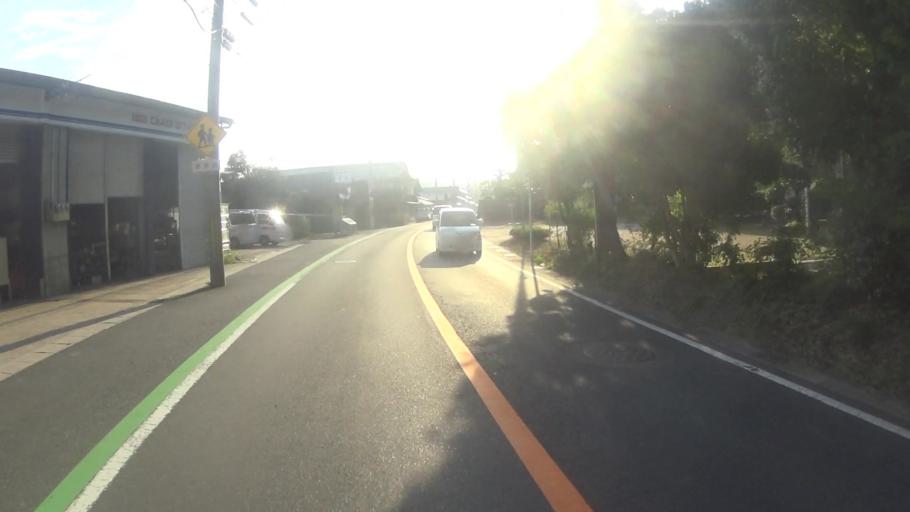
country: JP
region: Kyoto
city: Miyazu
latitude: 35.6349
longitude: 135.0792
